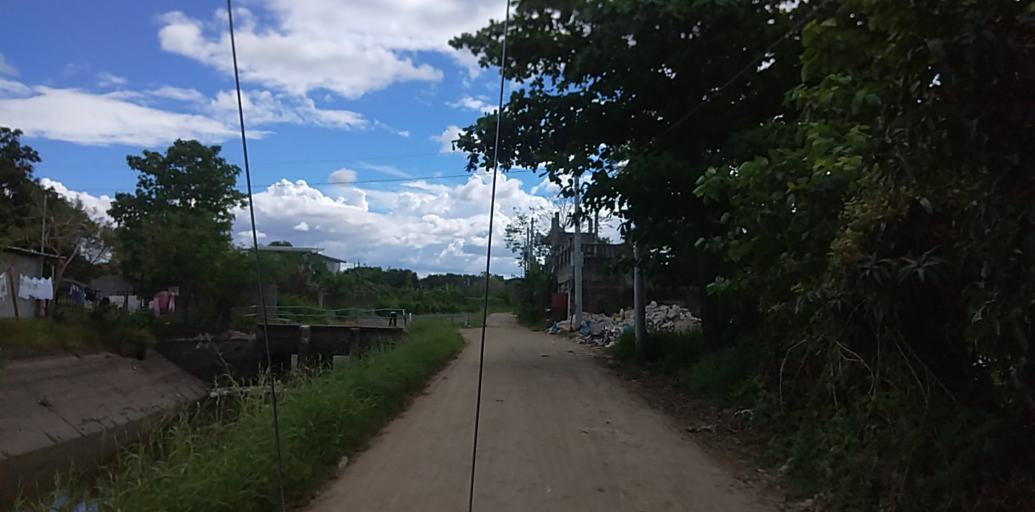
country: PH
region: Central Luzon
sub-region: Province of Pampanga
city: Arayat
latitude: 15.1353
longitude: 120.7788
